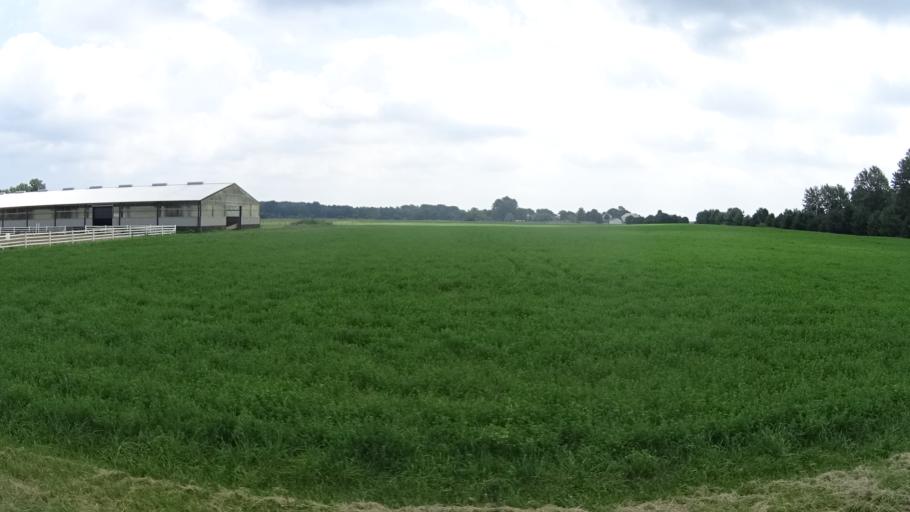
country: US
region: Ohio
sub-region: Lorain County
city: Vermilion
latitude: 41.3693
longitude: -82.3807
